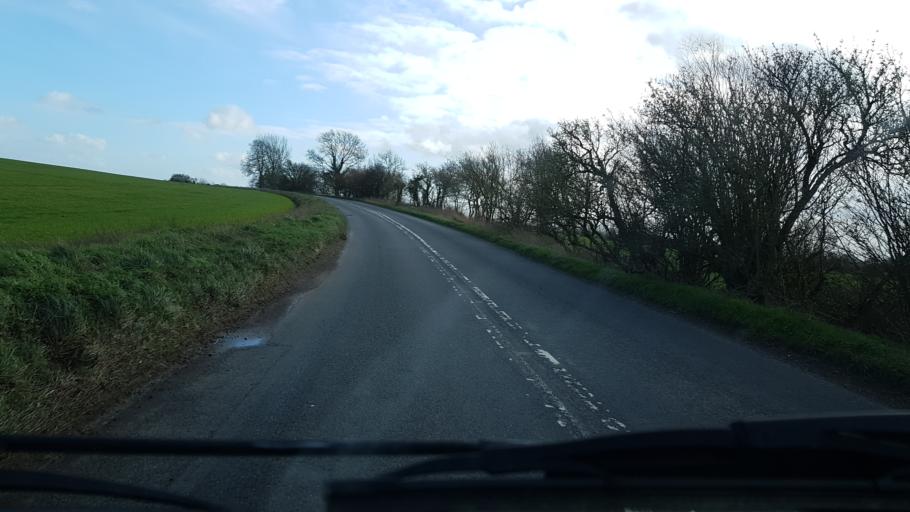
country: GB
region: England
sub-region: Wiltshire
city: Avebury
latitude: 51.4661
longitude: -1.8493
